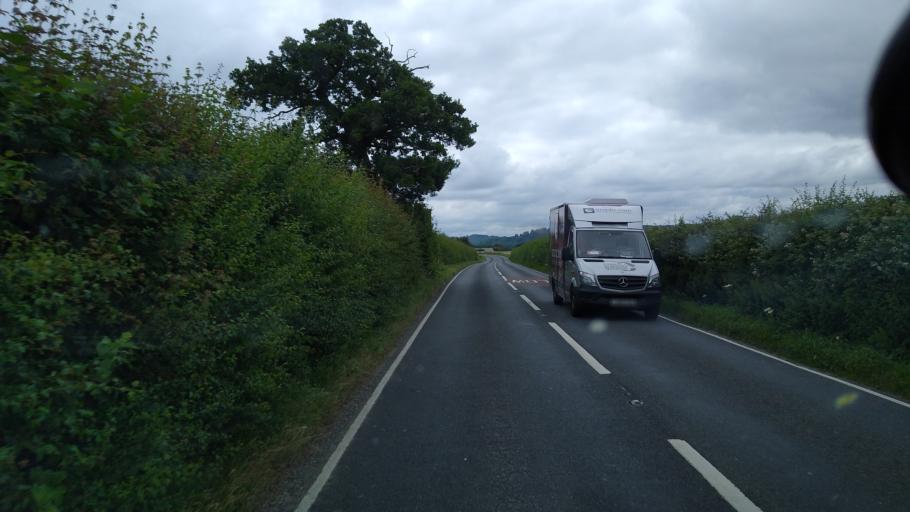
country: GB
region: England
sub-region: Hampshire
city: Alton
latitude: 51.1227
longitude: -0.9510
